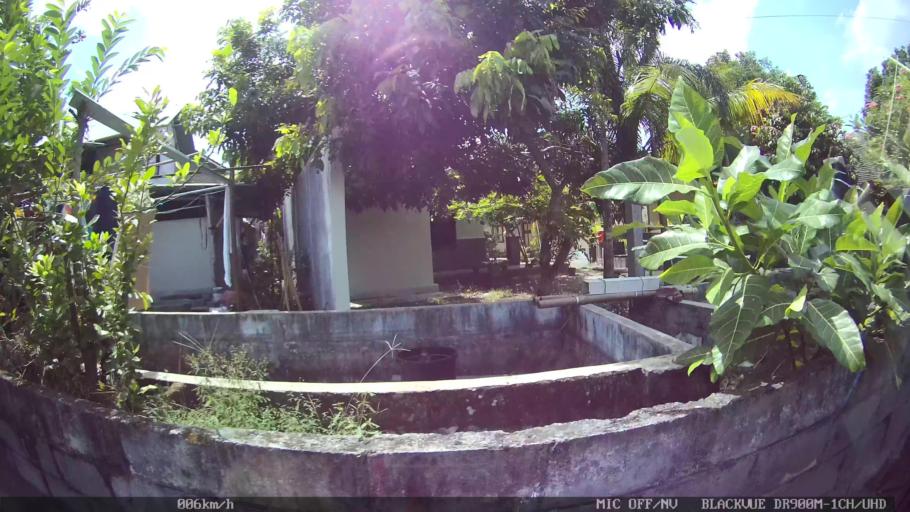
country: ID
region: Daerah Istimewa Yogyakarta
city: Kasihan
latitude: -7.8224
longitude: 110.3526
